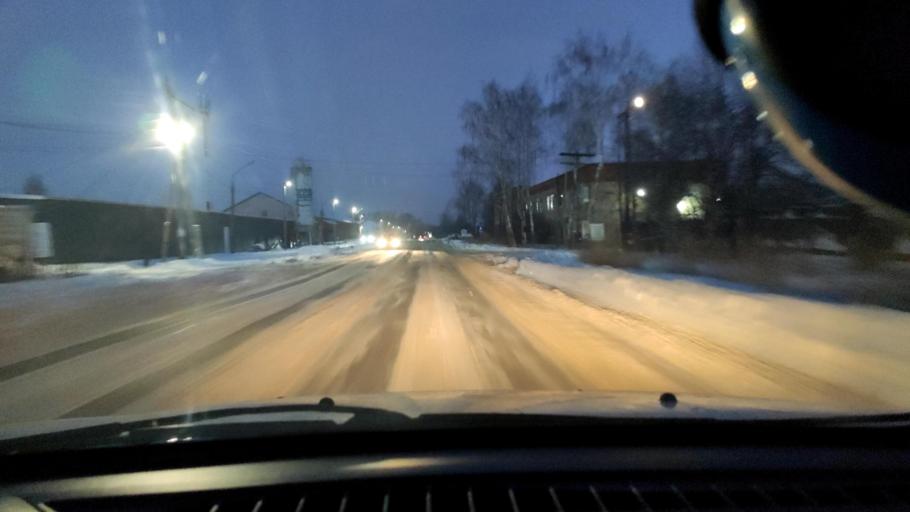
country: RU
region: Perm
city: Kultayevo
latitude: 57.8900
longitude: 55.9280
